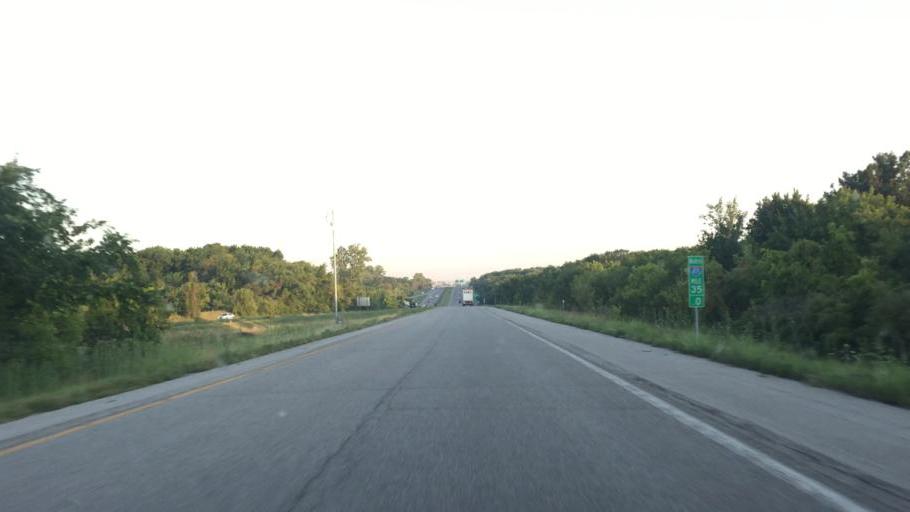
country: US
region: Missouri
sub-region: Platte County
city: Weatherby Lake
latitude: 39.3201
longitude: -94.6947
